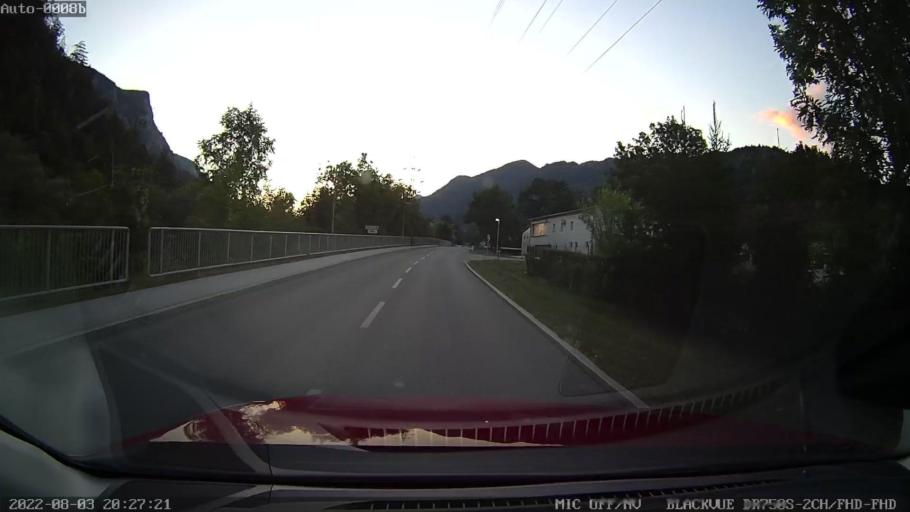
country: SI
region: Jesenice
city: Hrusica
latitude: 46.4382
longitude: 14.0373
